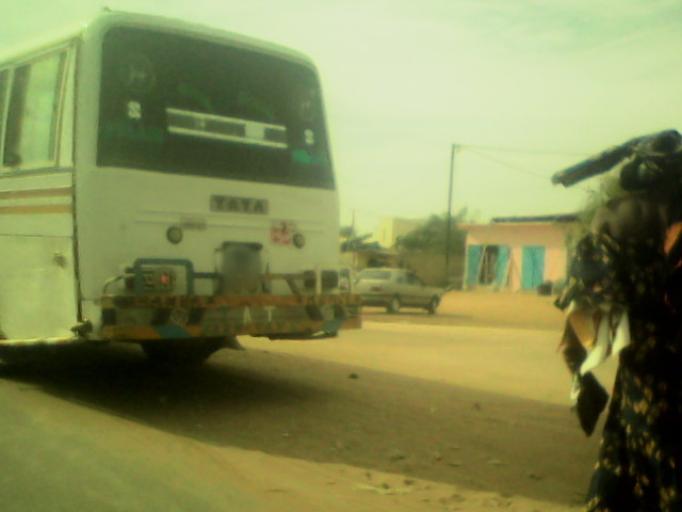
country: SN
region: Diourbel
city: Touba
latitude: 14.8850
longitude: -15.8761
